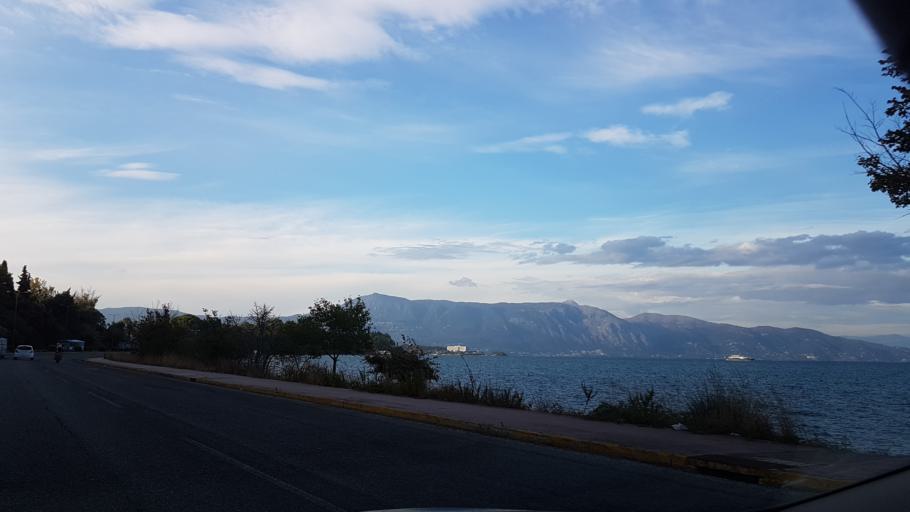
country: GR
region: Ionian Islands
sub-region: Nomos Kerkyras
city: Kontokali
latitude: 39.6414
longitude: 19.8631
